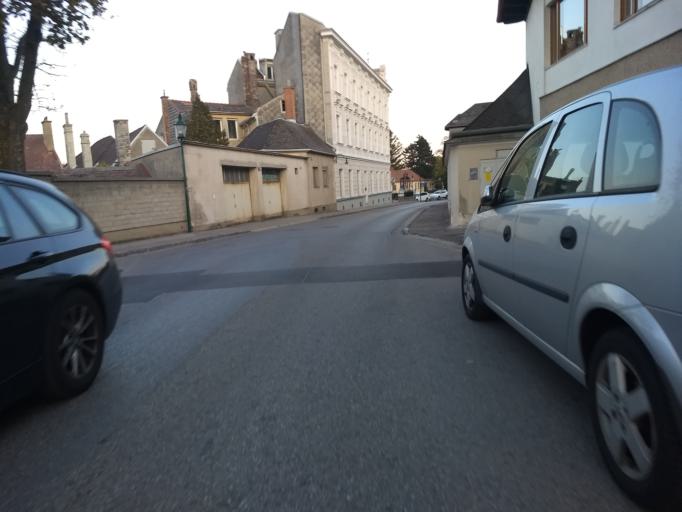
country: AT
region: Lower Austria
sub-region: Politischer Bezirk Modling
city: Perchtoldsdorf
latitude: 48.1221
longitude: 16.2626
